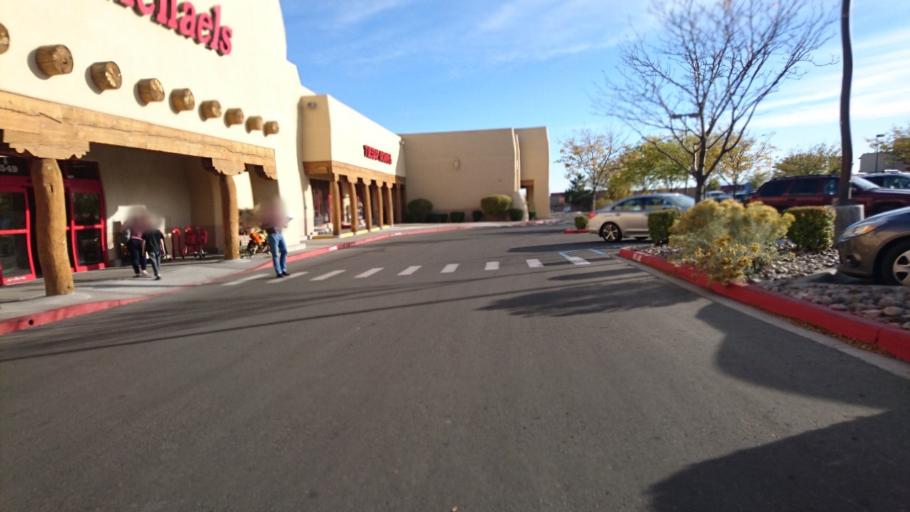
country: US
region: New Mexico
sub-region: Santa Fe County
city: Agua Fria
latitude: 35.6399
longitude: -106.0107
